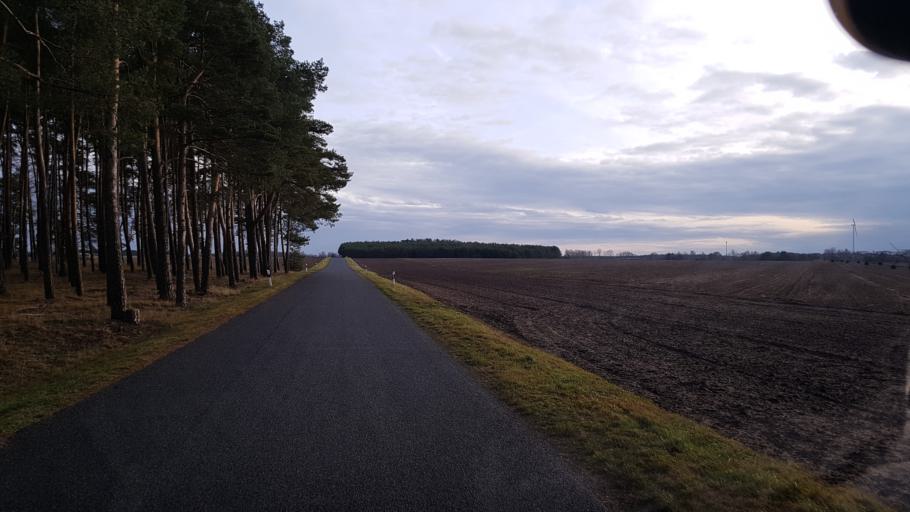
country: DE
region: Brandenburg
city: Bronkow
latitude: 51.6608
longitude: 13.8813
